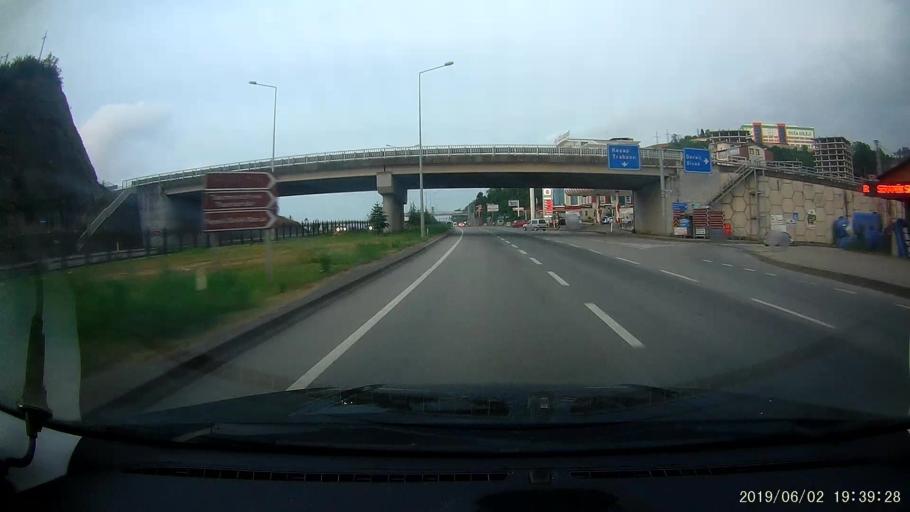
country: TR
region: Giresun
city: Giresun
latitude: 40.9132
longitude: 38.4415
